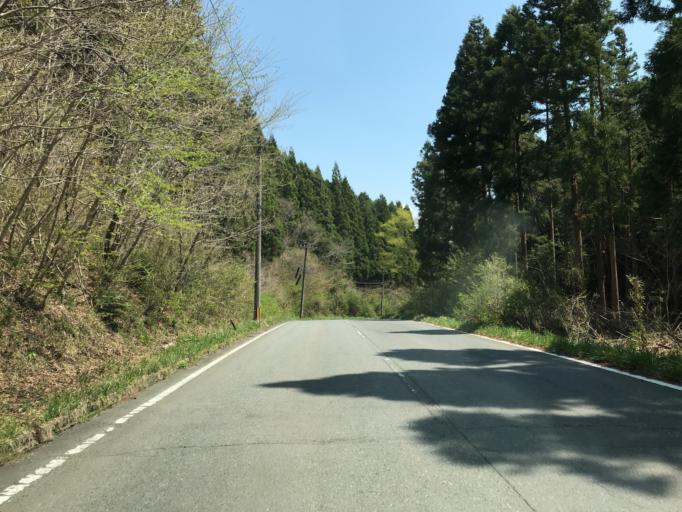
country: JP
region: Ibaraki
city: Kitaibaraki
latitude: 36.9767
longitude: 140.6301
